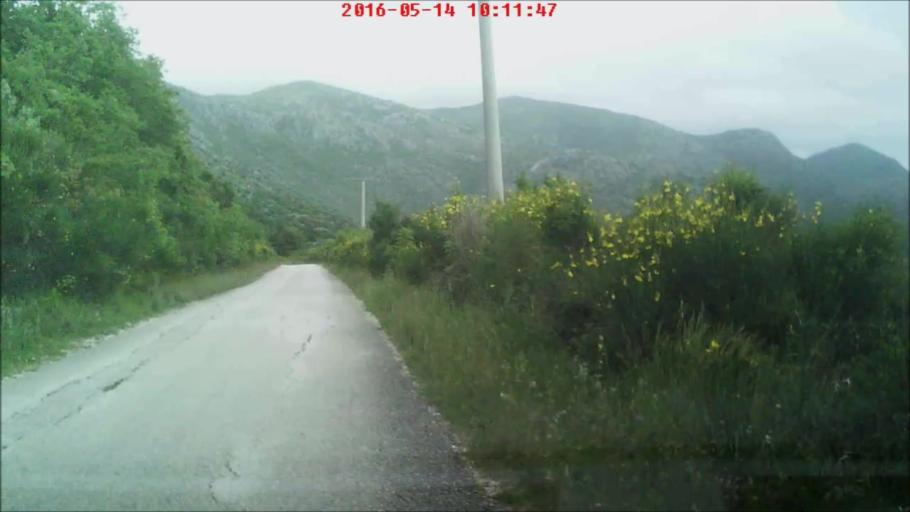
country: HR
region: Dubrovacko-Neretvanska
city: Podgora
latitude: 42.7354
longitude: 17.9450
